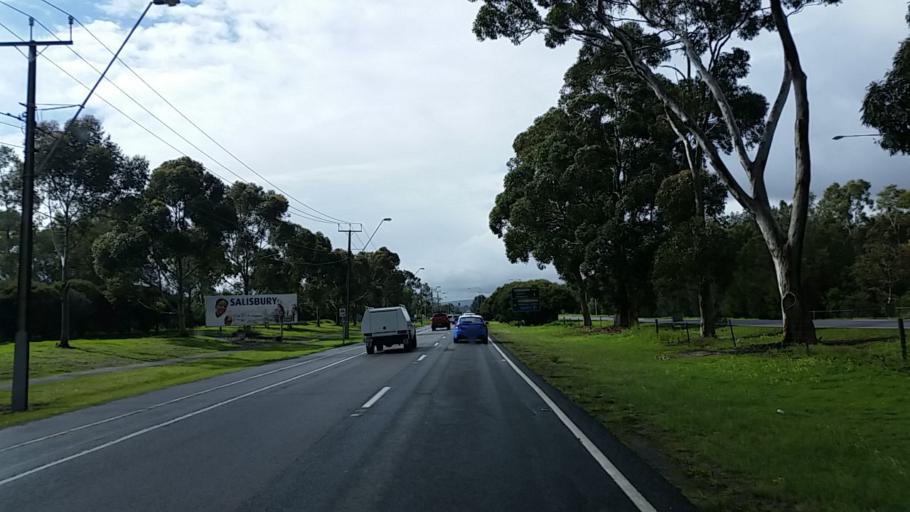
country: AU
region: South Australia
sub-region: Salisbury
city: Ingle Farm
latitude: -34.8188
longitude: 138.6227
